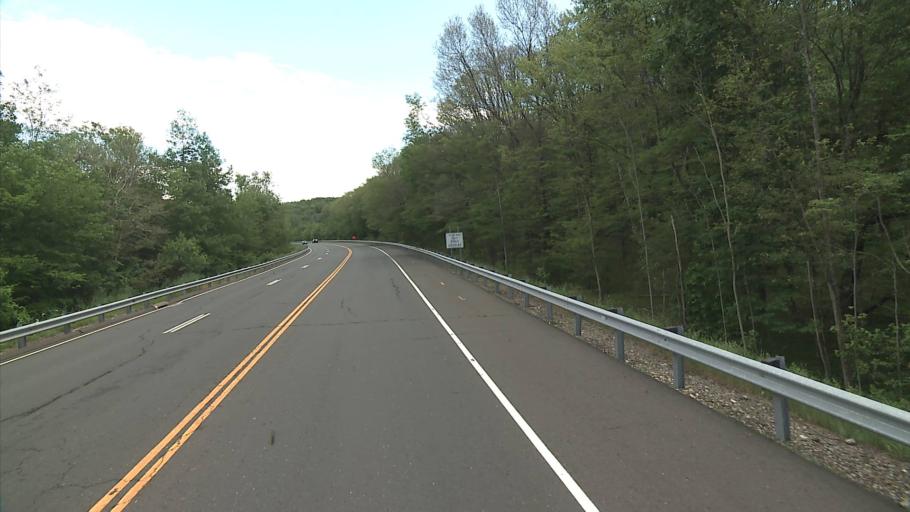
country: US
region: Connecticut
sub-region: New Haven County
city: Naugatuck
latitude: 41.5160
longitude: -73.0745
